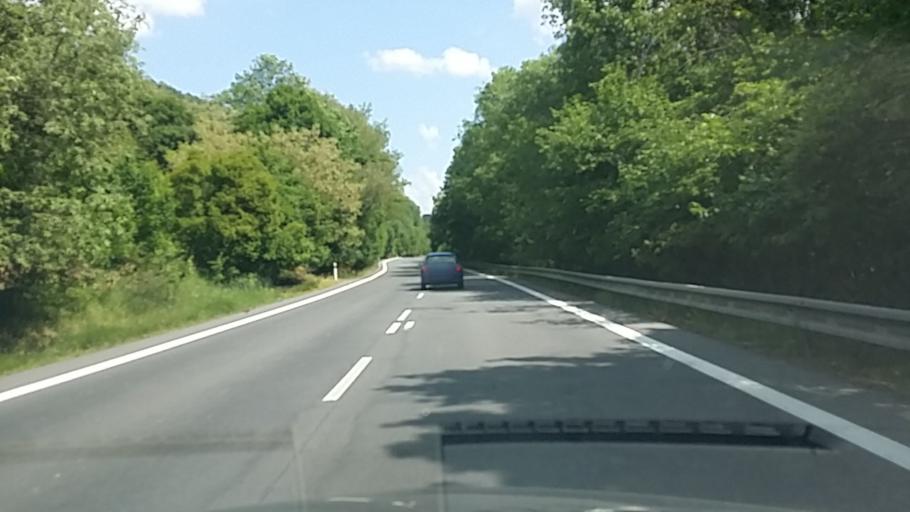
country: SK
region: Banskobystricky
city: Dudince
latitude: 48.2492
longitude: 18.9696
